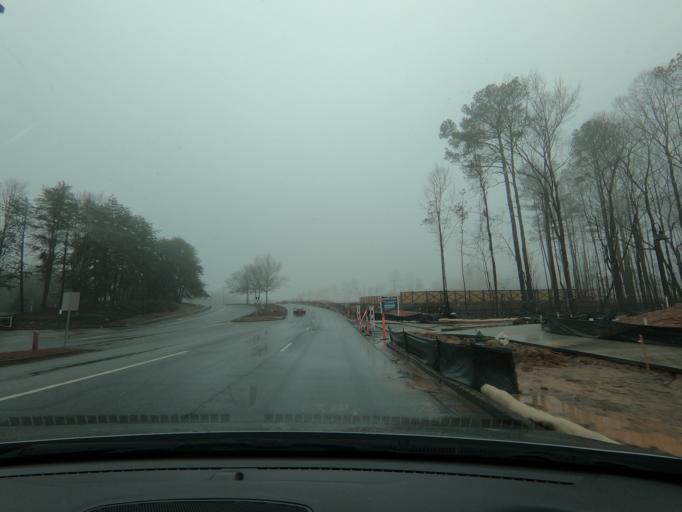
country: US
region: Georgia
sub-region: Fulton County
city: Alpharetta
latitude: 34.0840
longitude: -84.2586
